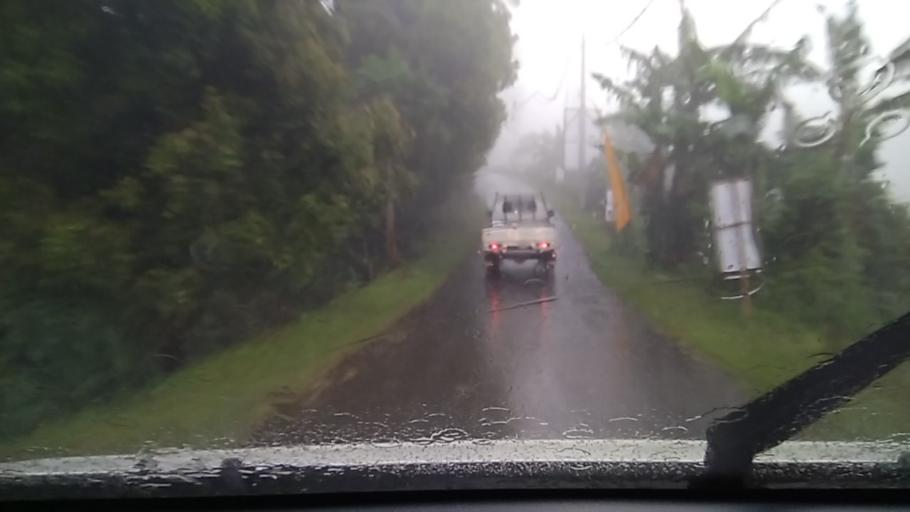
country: ID
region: Bali
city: Banjar Ambengan
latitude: -8.2095
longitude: 115.1719
